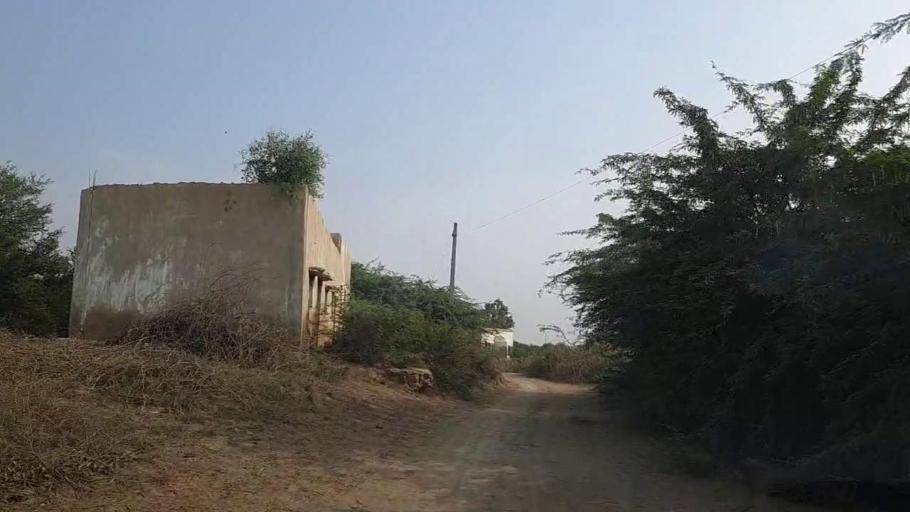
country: PK
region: Sindh
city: Gharo
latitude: 24.6539
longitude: 67.6185
